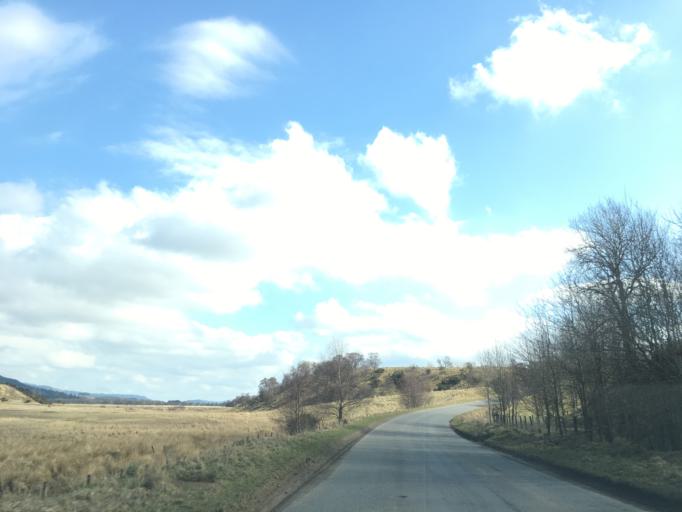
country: GB
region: Scotland
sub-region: Highland
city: Kingussie
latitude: 57.0719
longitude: -4.0306
